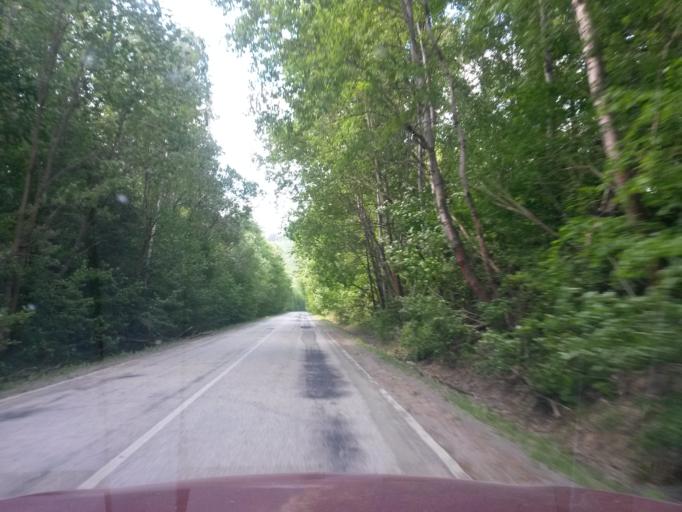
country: SK
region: Kosicky
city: Moldava nad Bodvou
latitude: 48.7299
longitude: 21.0870
